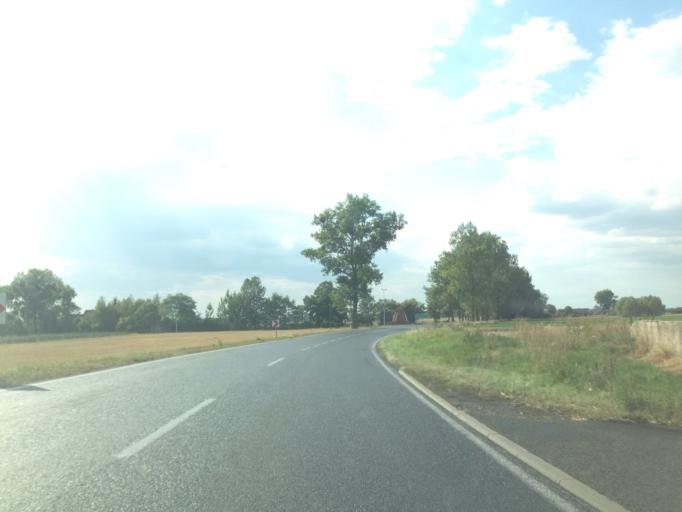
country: PL
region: Kujawsko-Pomorskie
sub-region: Powiat swiecki
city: Bukowiec
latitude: 53.4542
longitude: 18.2044
